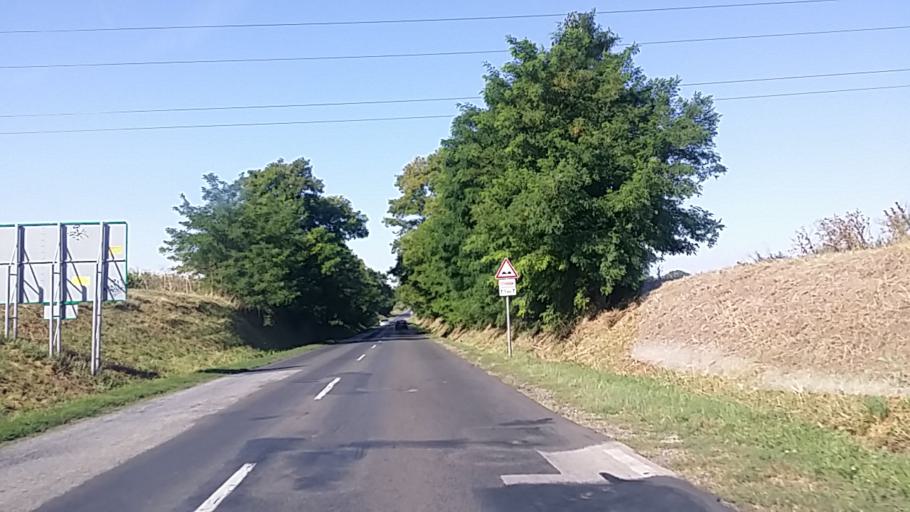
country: HU
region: Fejer
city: dunaujvaros
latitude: 46.9647
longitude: 18.8854
